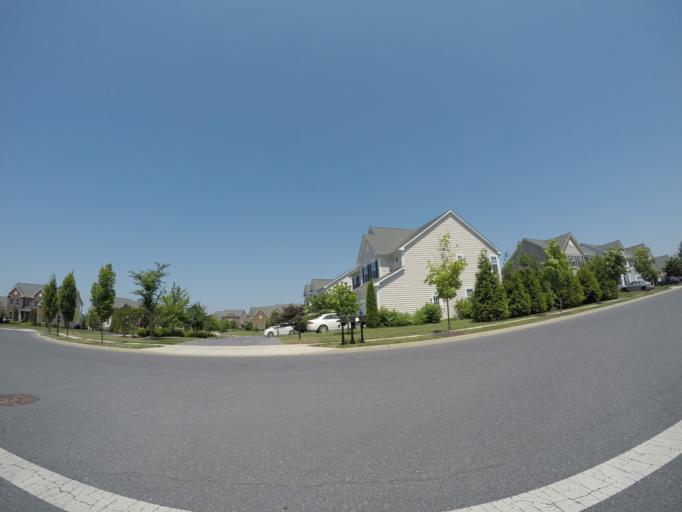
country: US
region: Maryland
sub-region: Frederick County
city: Urbana
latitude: 39.3363
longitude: -77.3589
